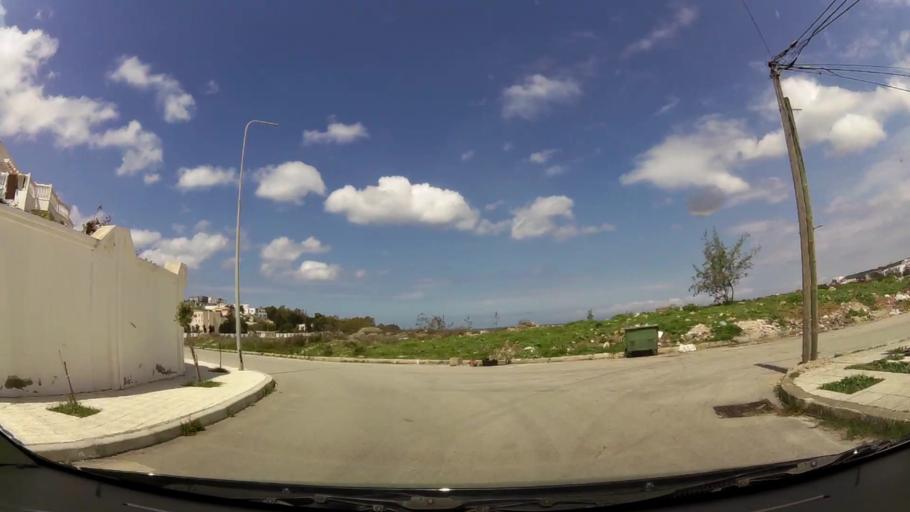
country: MA
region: Tanger-Tetouan
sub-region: Tanger-Assilah
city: Tangier
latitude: 35.7733
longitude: -5.7672
